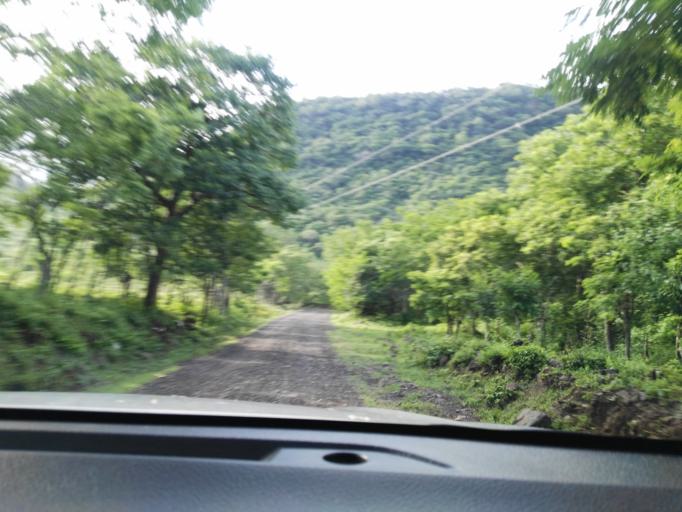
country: NI
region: Matagalpa
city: Terrabona
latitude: 12.8473
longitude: -86.0400
